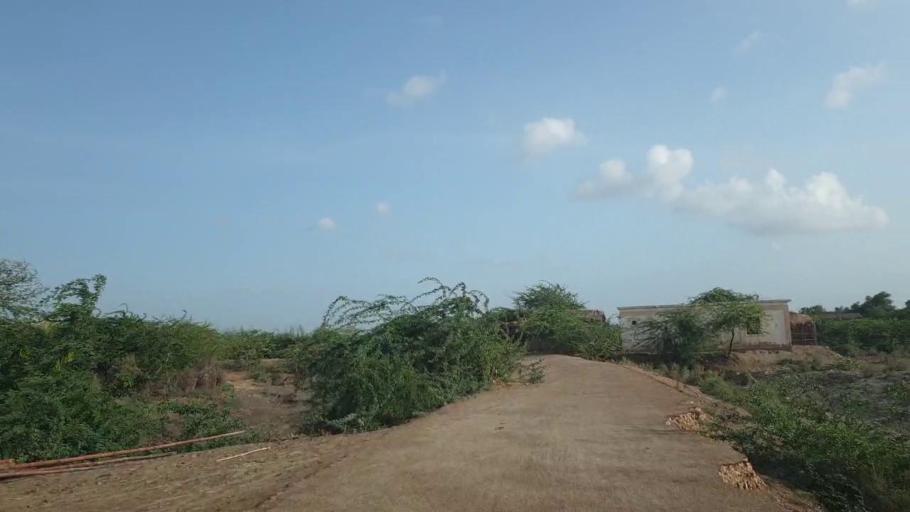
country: PK
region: Sindh
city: Kadhan
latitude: 24.6384
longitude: 69.1050
